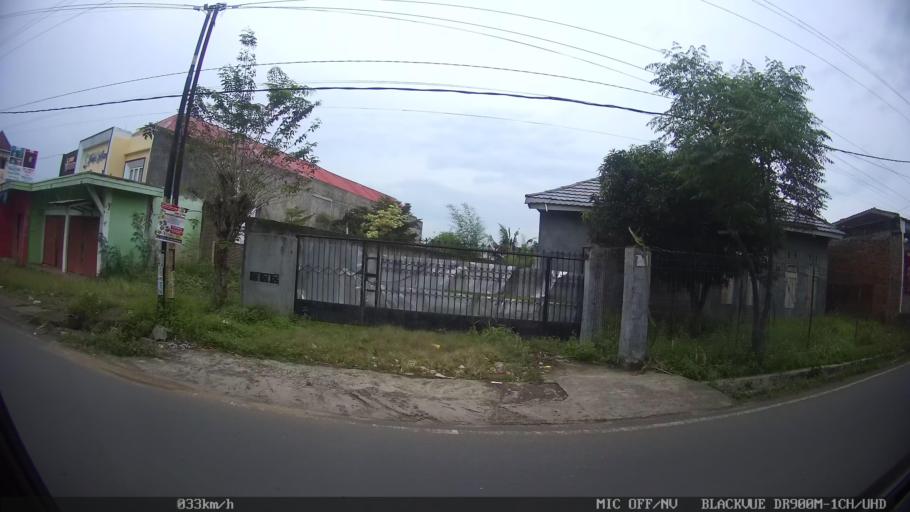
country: ID
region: Lampung
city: Kedaton
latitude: -5.3893
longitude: 105.2398
